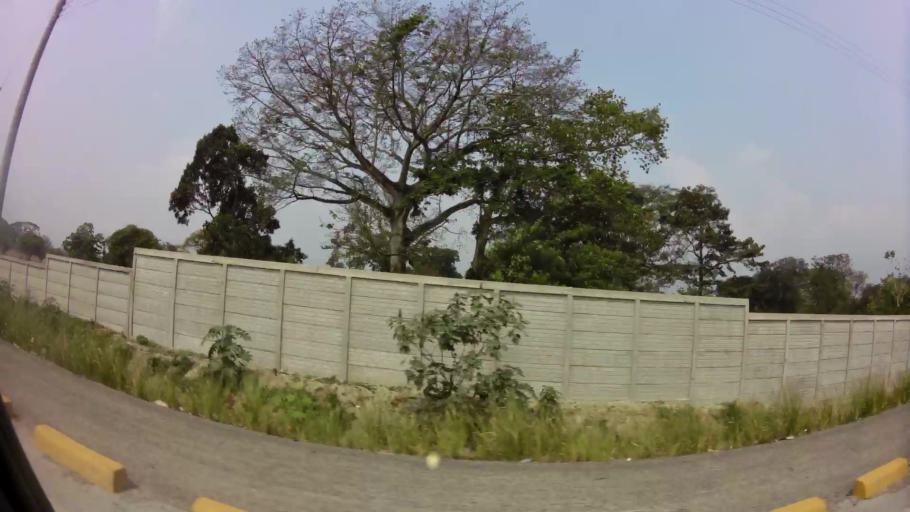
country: HN
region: Cortes
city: San Pedro Sula
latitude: 15.5228
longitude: -88.0027
